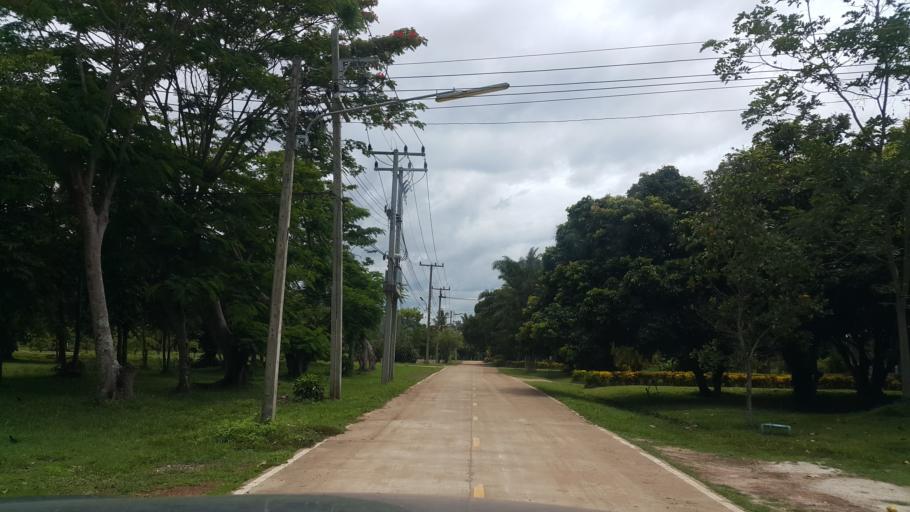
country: TH
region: Chiang Mai
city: Mae Taeng
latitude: 19.1687
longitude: 98.9510
